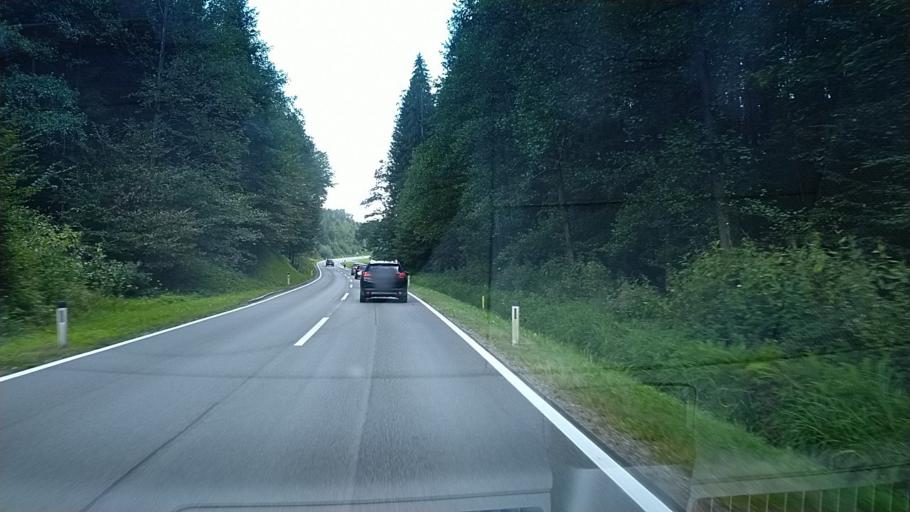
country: AT
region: Styria
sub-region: Politischer Bezirk Deutschlandsberg
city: Sankt Peter im Sulmtal
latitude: 46.7472
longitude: 15.2294
